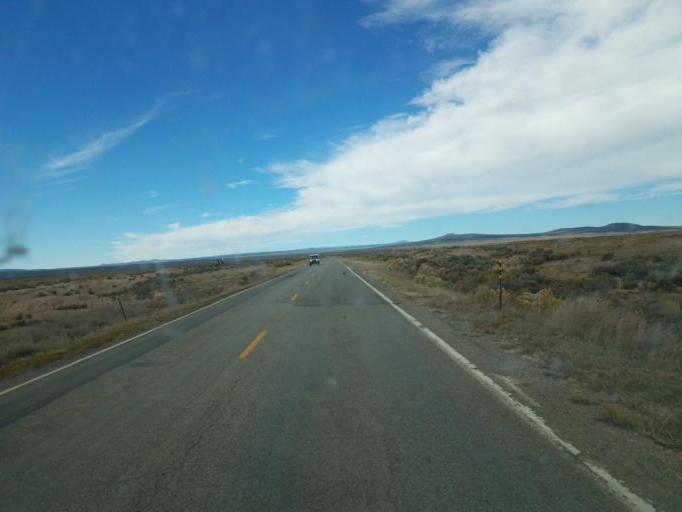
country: US
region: New Mexico
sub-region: Taos County
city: Arroyo Seco
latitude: 36.4694
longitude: -105.6901
